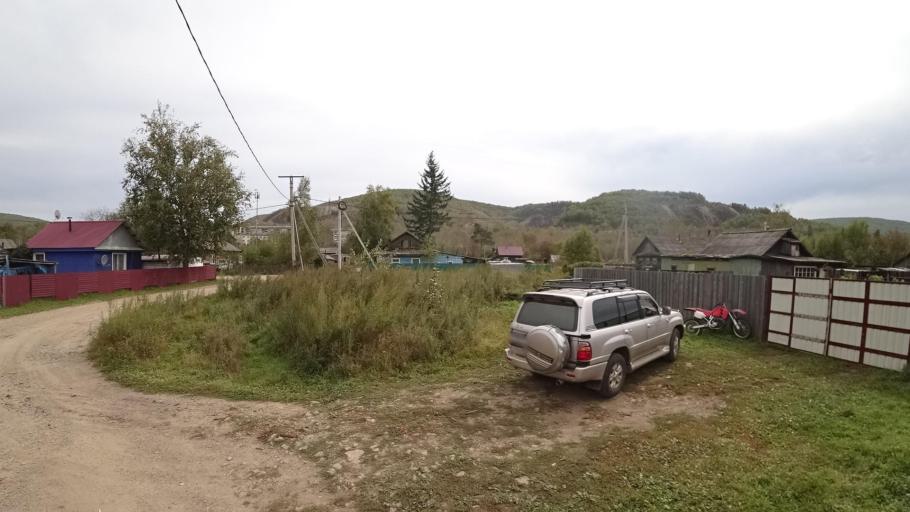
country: RU
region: Jewish Autonomous Oblast
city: Khingansk
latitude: 49.1288
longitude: 131.1869
